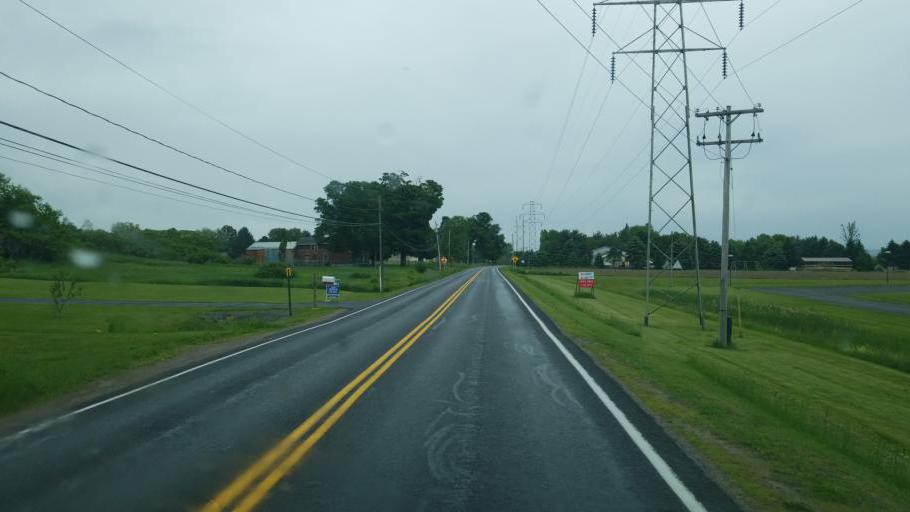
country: US
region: New York
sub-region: Oneida County
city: Utica
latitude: 43.1110
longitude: -75.1466
